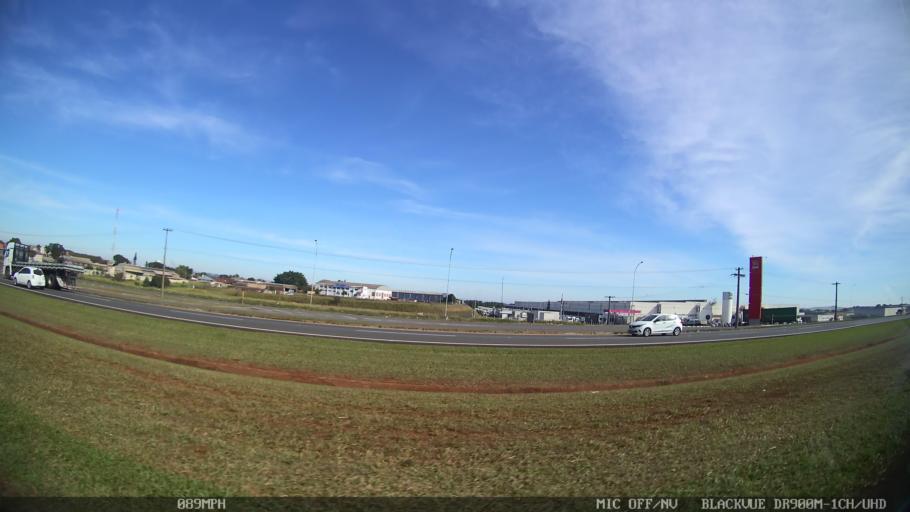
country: BR
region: Sao Paulo
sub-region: Cordeiropolis
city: Cordeiropolis
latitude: -22.4936
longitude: -47.3993
